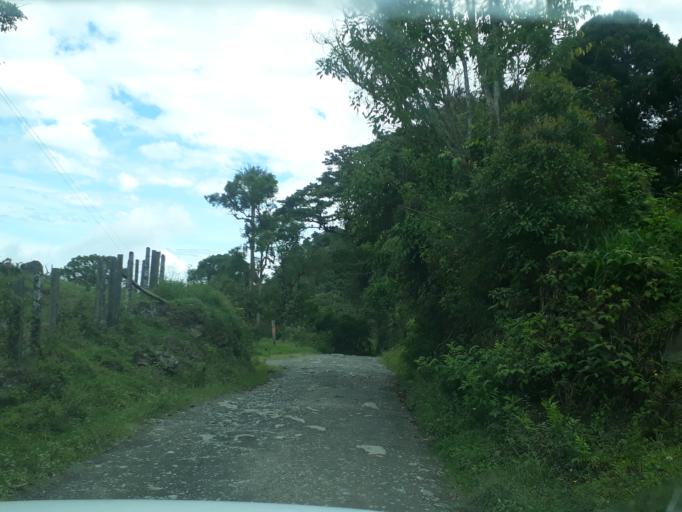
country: CO
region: Cundinamarca
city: Carmen de Carupa
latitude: 5.3562
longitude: -74.0685
